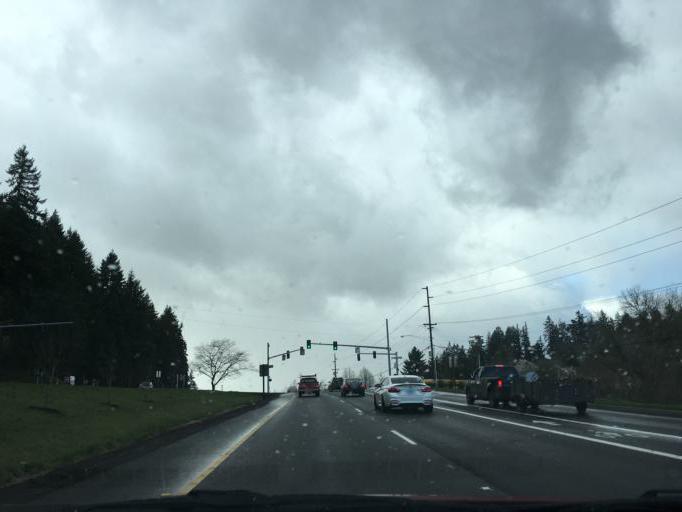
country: US
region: Oregon
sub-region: Washington County
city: King City
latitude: 45.4156
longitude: -122.7908
